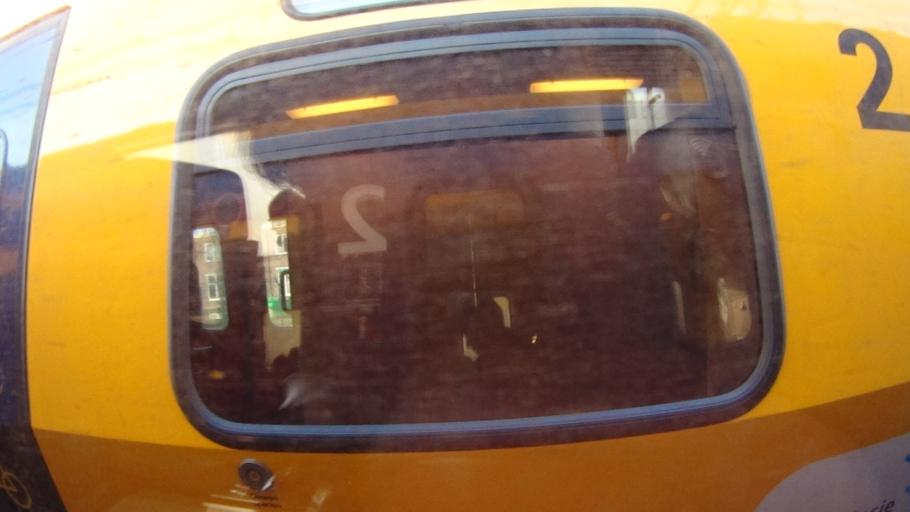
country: NL
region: Overijssel
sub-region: Gemeente Zwolle
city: Zwolle
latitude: 52.5066
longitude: 6.0869
